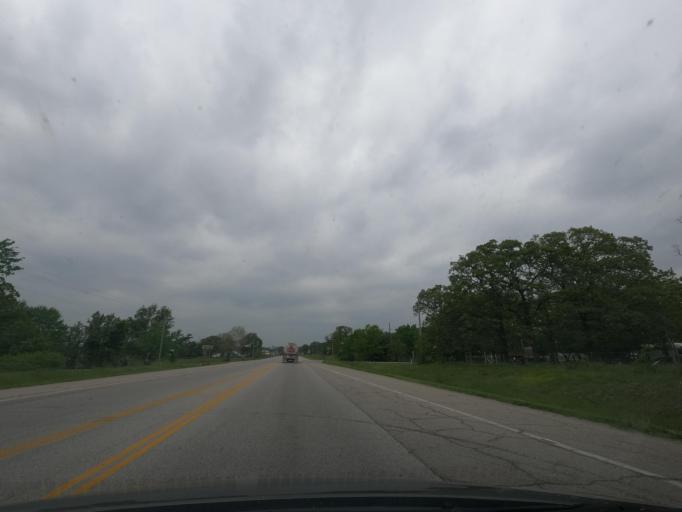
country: US
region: Kansas
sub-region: Cherokee County
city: Galena
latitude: 37.0237
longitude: -94.6438
